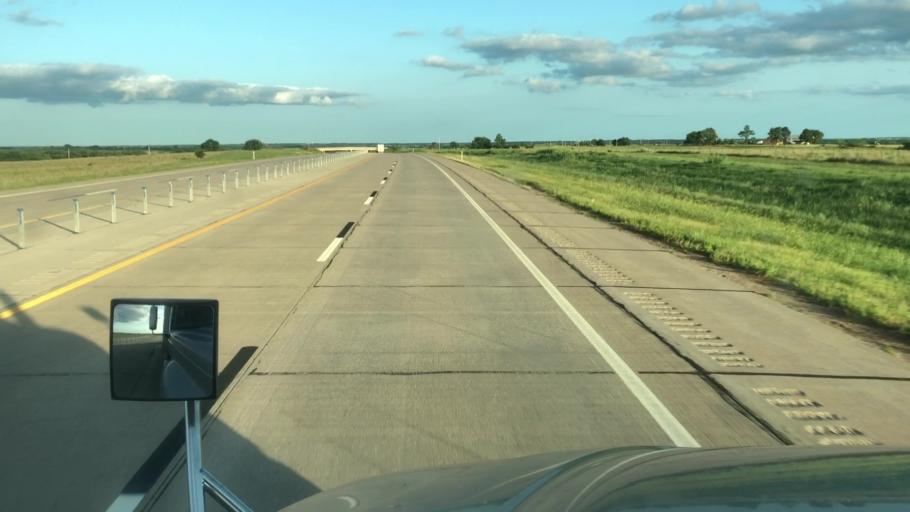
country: US
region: Oklahoma
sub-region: Pawnee County
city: Pawnee
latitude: 36.3378
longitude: -97.0208
